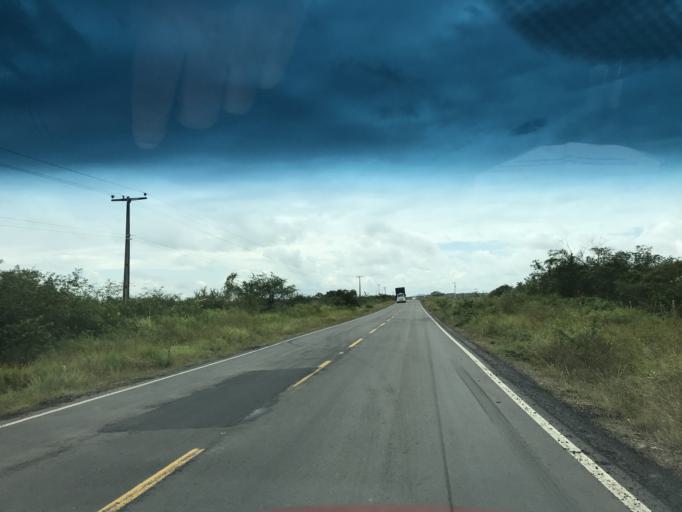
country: BR
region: Bahia
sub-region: Castro Alves
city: Castro Alves
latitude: -12.6829
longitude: -39.3064
